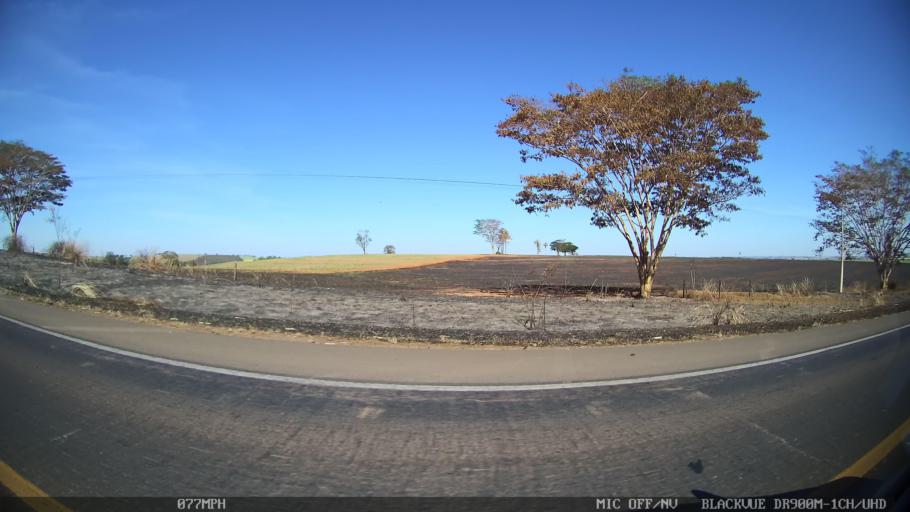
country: BR
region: Sao Paulo
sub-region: Olimpia
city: Olimpia
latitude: -20.6626
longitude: -48.8627
